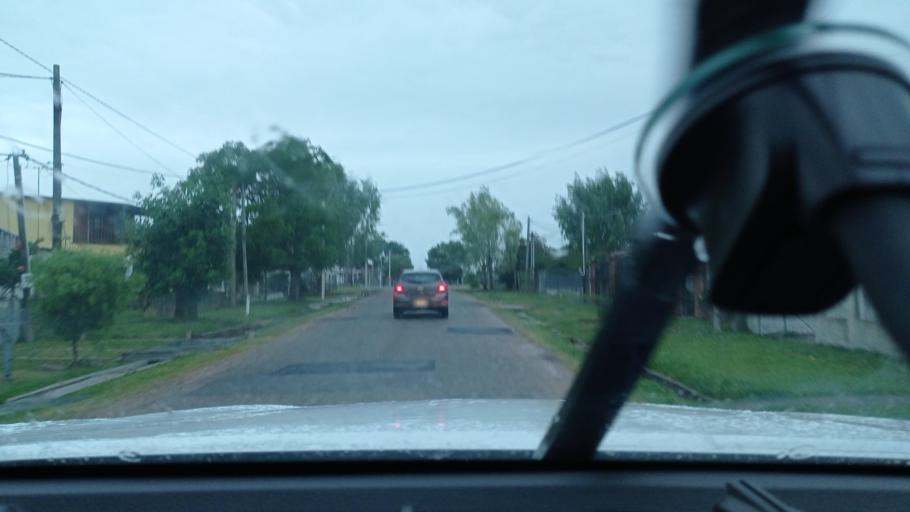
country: UY
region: Canelones
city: Joaquin Suarez
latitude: -34.7559
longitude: -56.0136
